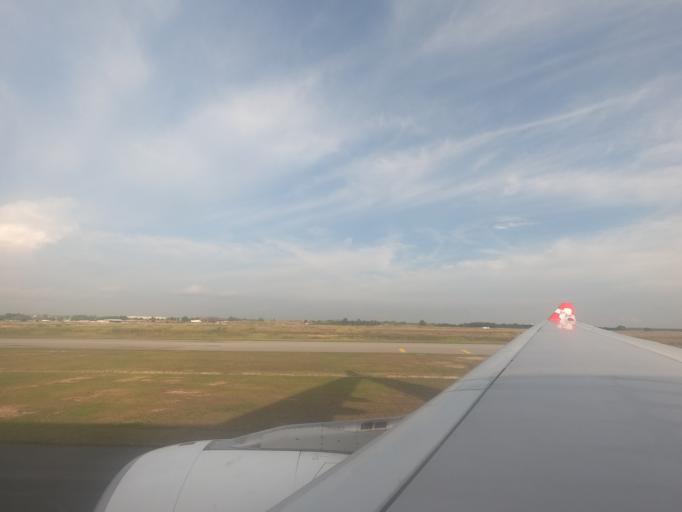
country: MY
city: Sungai Pelek New Village
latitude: 2.7378
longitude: 101.6894
